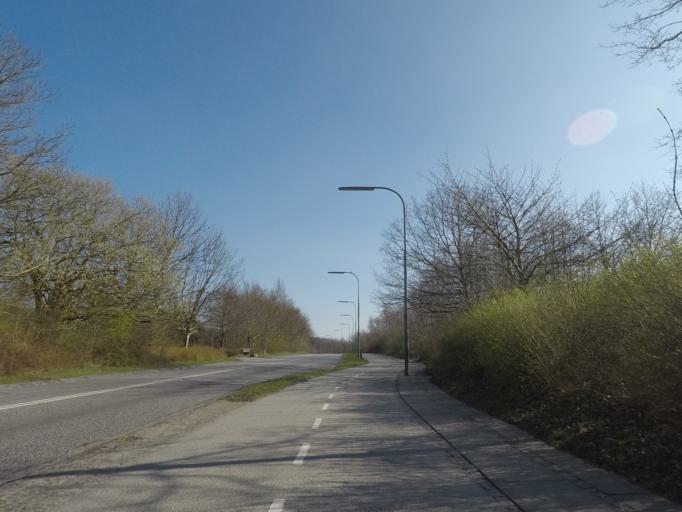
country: DK
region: Capital Region
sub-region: Ballerup Kommune
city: Ballerup
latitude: 55.7474
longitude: 12.3836
